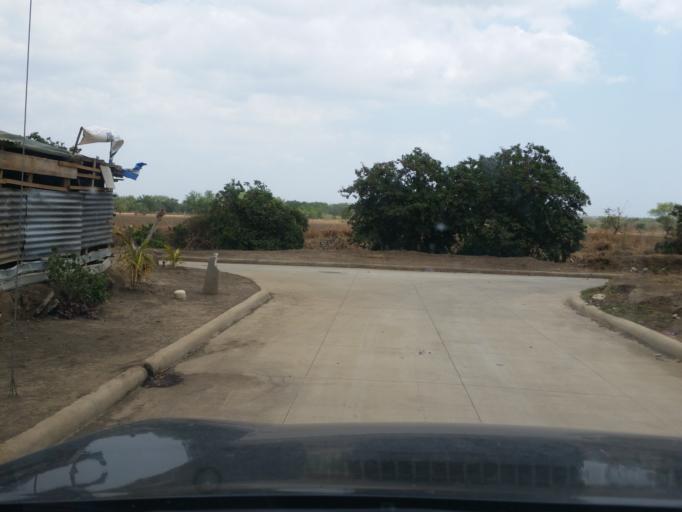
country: NI
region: Managua
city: Tipitapa
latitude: 12.1275
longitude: -86.1573
